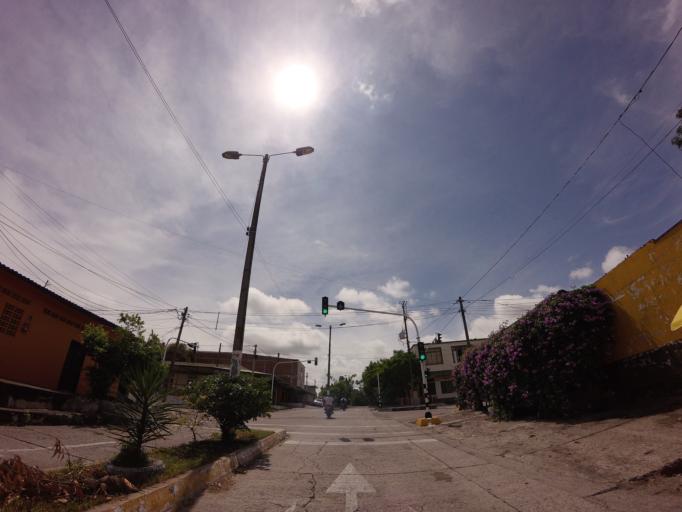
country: CO
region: Caldas
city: La Dorada
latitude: 5.4537
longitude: -74.6692
